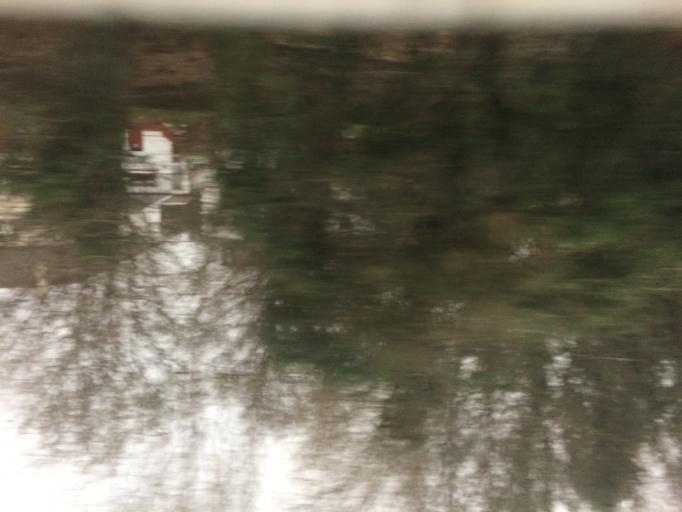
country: GB
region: Scotland
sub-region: East Renfrewshire
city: Giffnock
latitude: 55.7913
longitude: -4.3046
